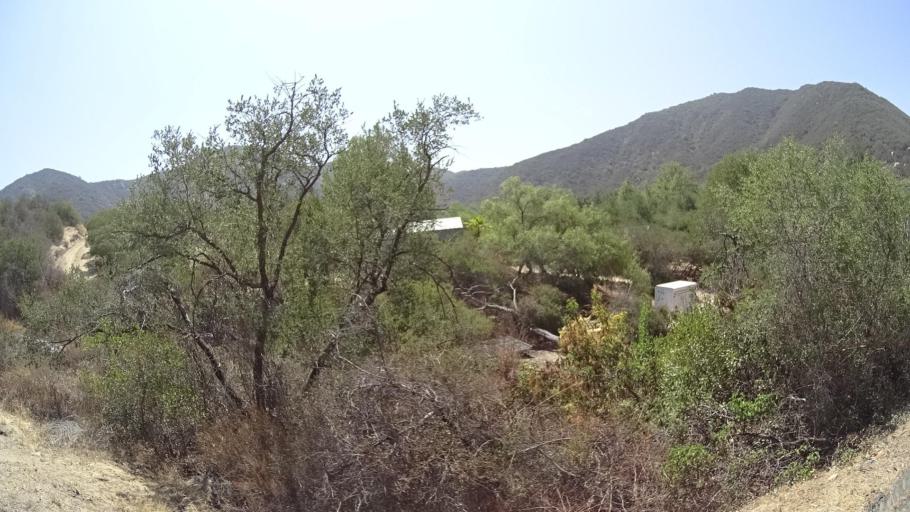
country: US
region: California
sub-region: San Diego County
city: Fallbrook
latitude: 33.4611
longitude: -117.2871
